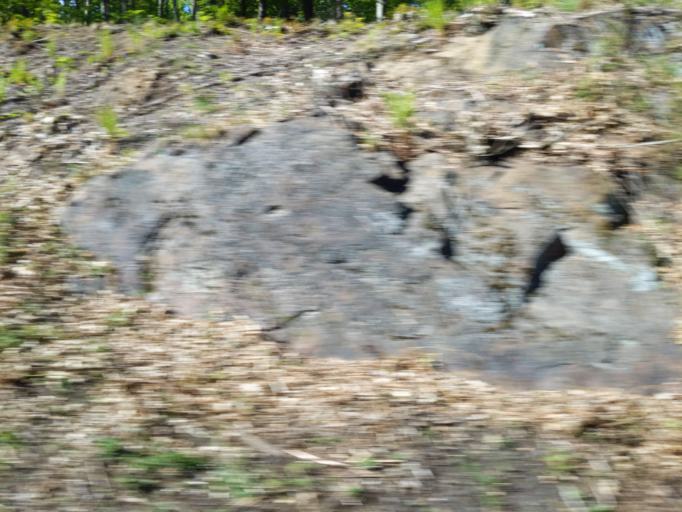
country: DE
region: Saxony
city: Radeberg
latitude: 51.1216
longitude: 13.8739
